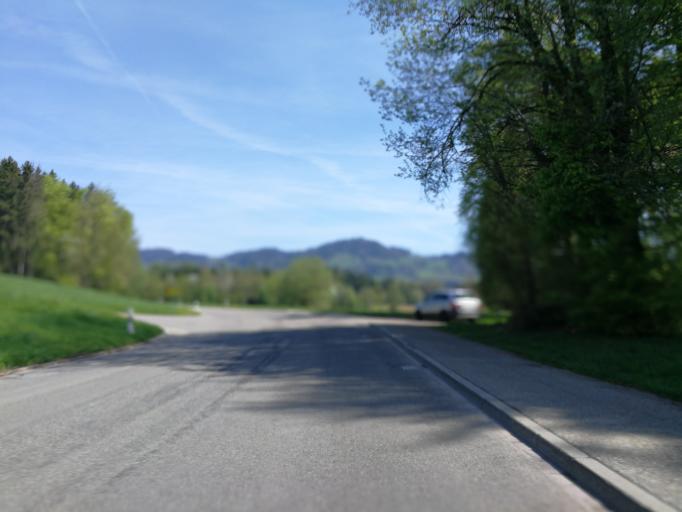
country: CH
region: Zurich
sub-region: Bezirk Hinwil
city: Hinwil
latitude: 47.2928
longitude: 8.8228
